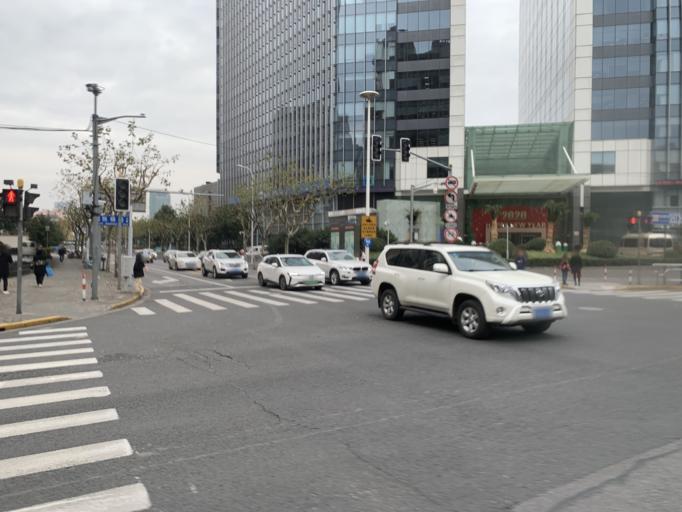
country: CN
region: Shanghai Shi
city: Pudong
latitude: 31.2310
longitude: 121.5182
